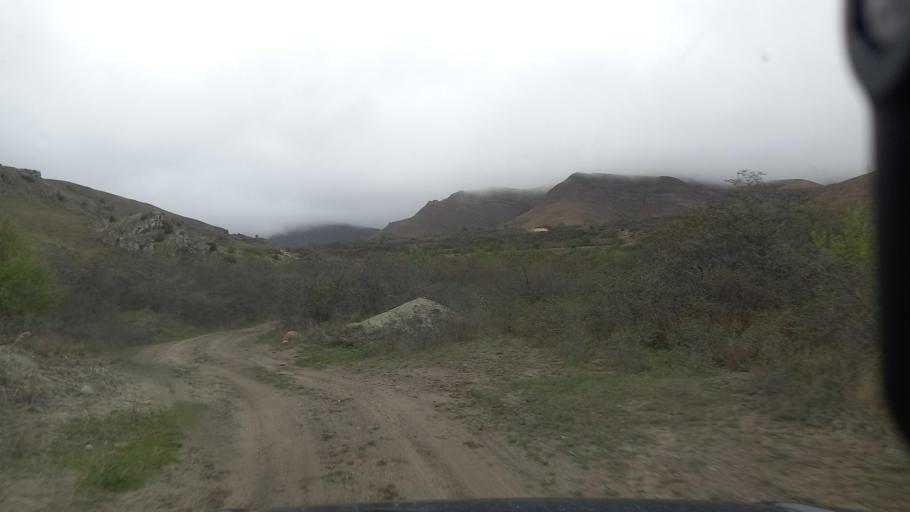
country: RU
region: Kabardino-Balkariya
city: Bylym
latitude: 43.4549
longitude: 43.0004
